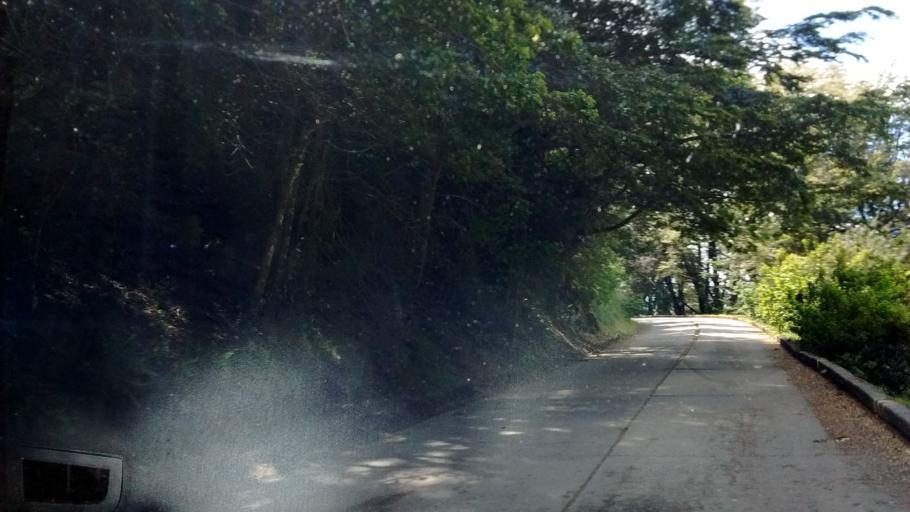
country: AR
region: Rio Negro
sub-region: Departamento de Bariloche
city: San Carlos de Bariloche
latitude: -41.0593
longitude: -71.5316
